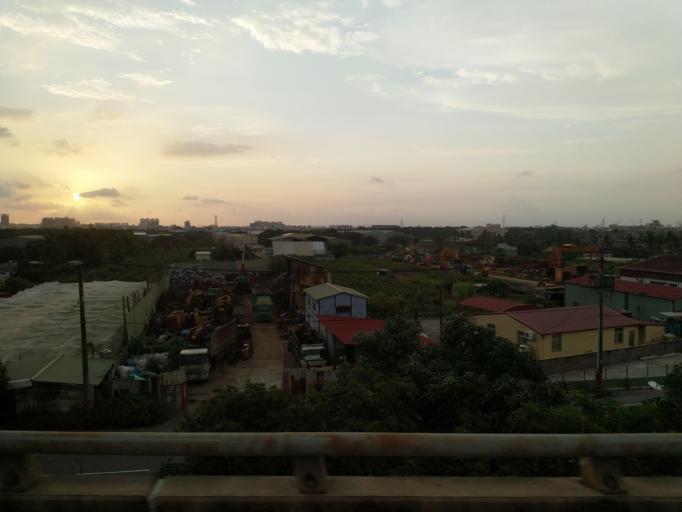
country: TW
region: Taiwan
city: Fengshan
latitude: 22.7470
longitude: 120.3629
